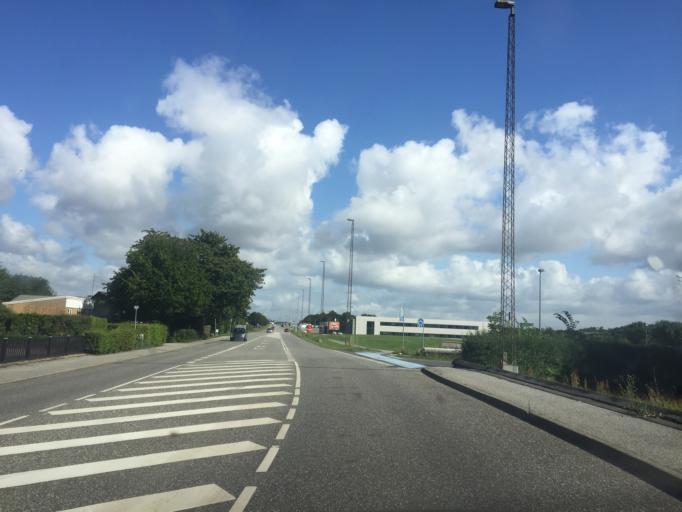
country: DK
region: South Denmark
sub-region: Fredericia Kommune
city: Snoghoj
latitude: 55.5264
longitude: 9.7168
